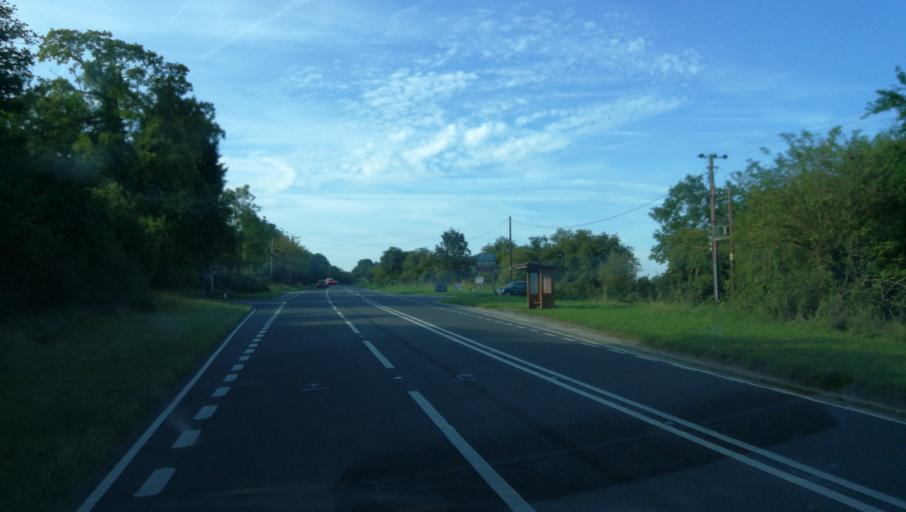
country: GB
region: England
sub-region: Oxfordshire
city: Deddington
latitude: 51.9553
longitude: -1.3180
